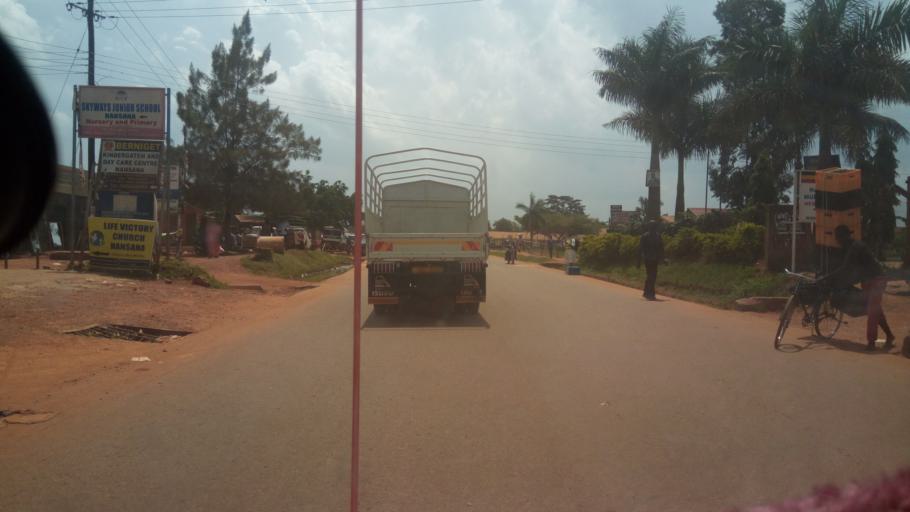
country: UG
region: Central Region
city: Kampala Central Division
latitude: 0.3637
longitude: 32.5288
